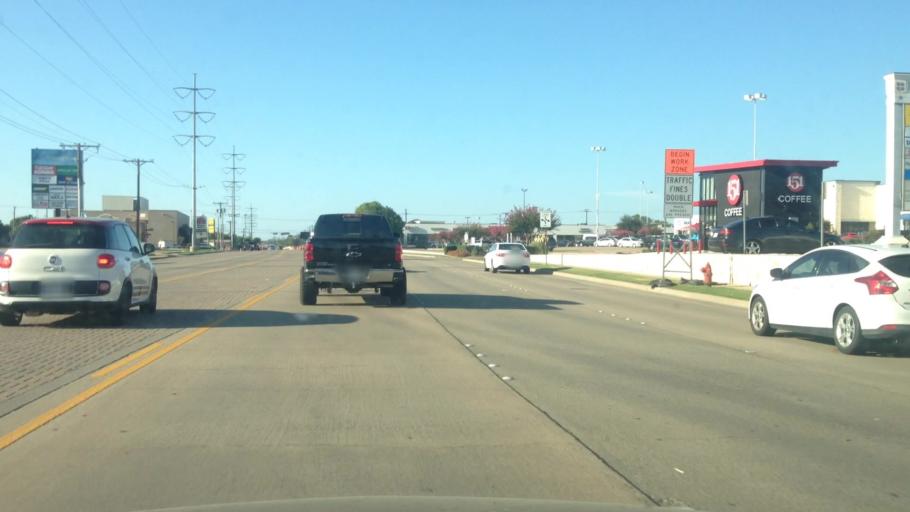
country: US
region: Texas
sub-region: Tarrant County
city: Watauga
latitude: 32.8575
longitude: -97.2382
